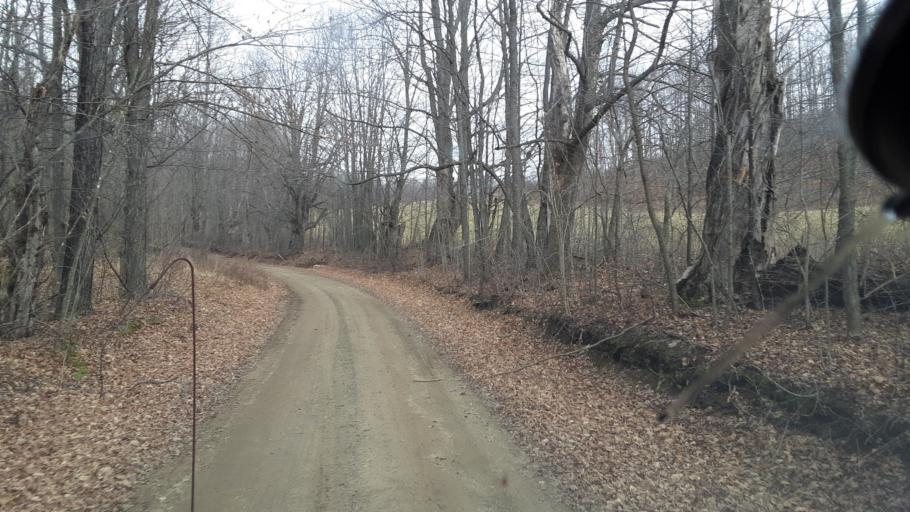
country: US
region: Pennsylvania
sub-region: Tioga County
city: Westfield
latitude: 41.9172
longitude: -77.7047
